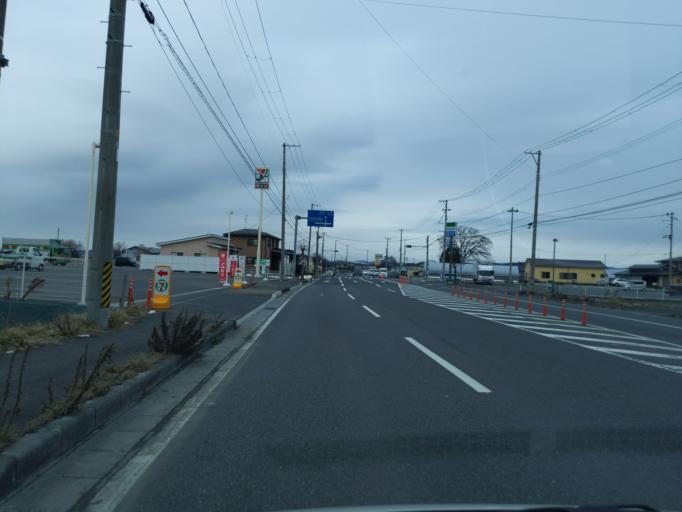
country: JP
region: Iwate
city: Mizusawa
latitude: 39.1752
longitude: 141.1589
